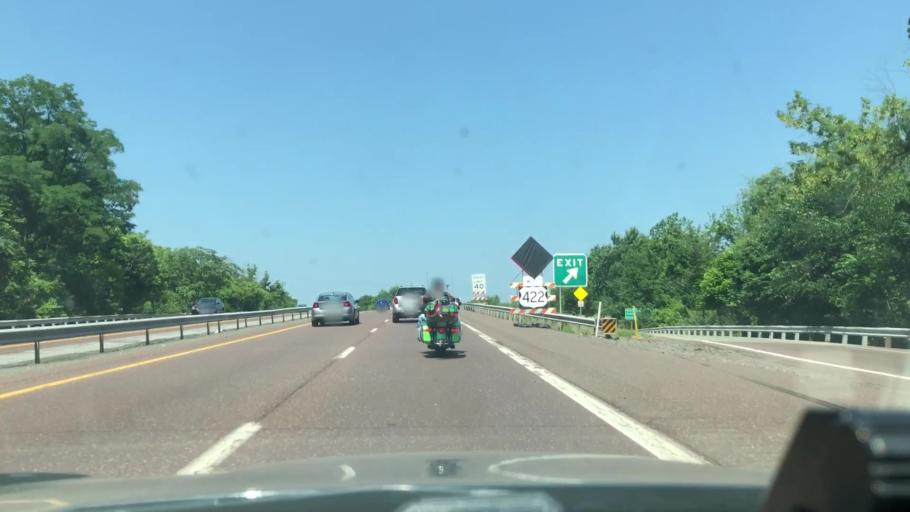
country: US
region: Pennsylvania
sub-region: Chester County
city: South Pottstown
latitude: 40.2381
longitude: -75.6495
